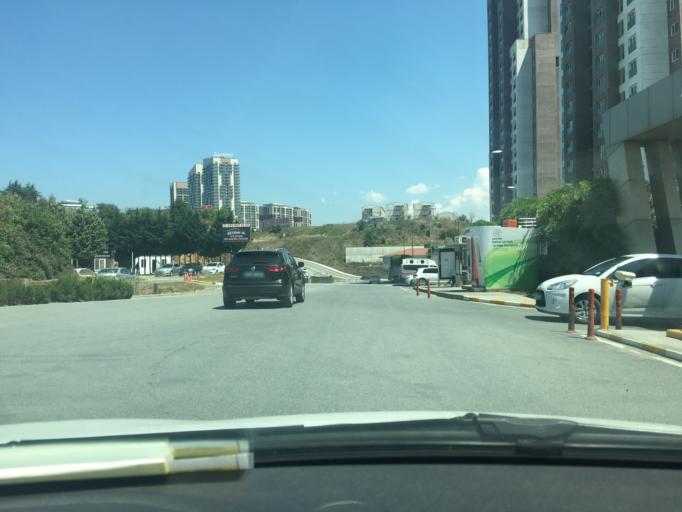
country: TR
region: Istanbul
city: Sisli
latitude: 41.0913
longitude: 28.9376
